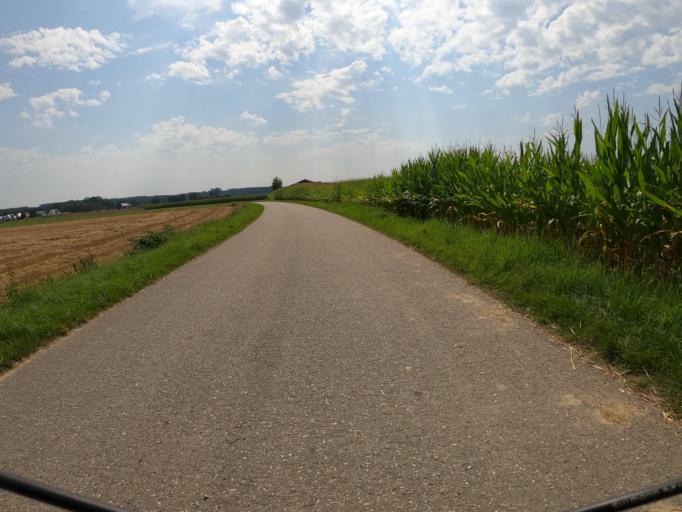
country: DE
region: Bavaria
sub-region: Swabia
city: Rieden an der Kotz
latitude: 48.3646
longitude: 10.2410
